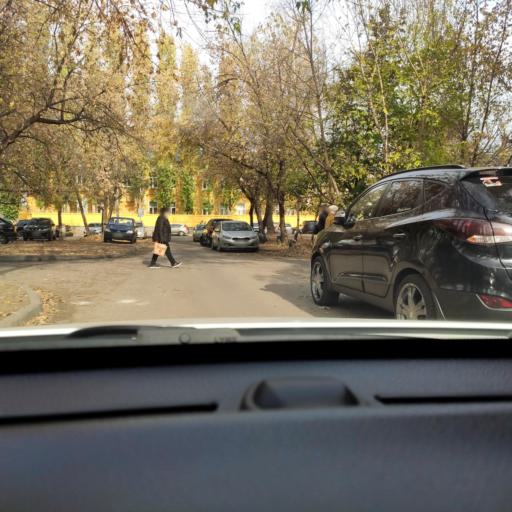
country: RU
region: Voronezj
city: Voronezh
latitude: 51.6743
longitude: 39.2466
